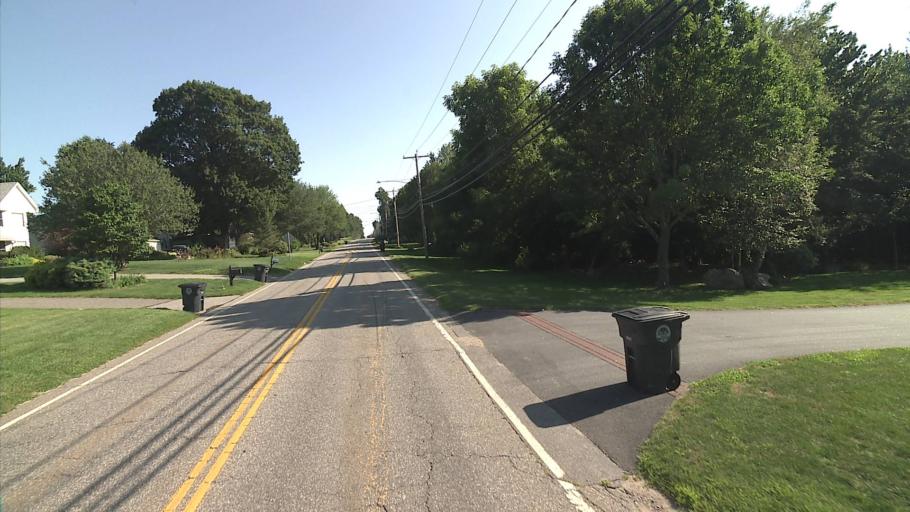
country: US
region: Connecticut
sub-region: Litchfield County
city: Northwest Harwinton
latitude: 41.8240
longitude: -73.0801
